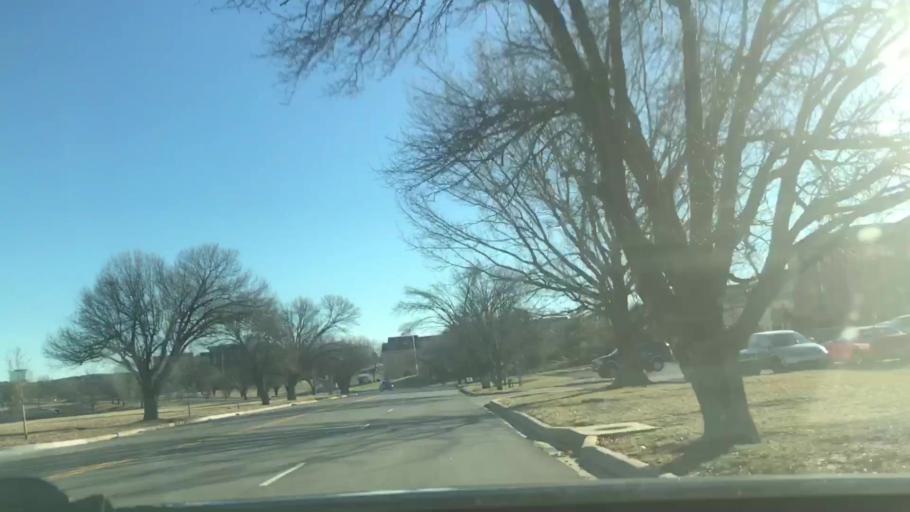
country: US
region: Missouri
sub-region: Platte County
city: Weatherby Lake
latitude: 39.2949
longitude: -94.6818
